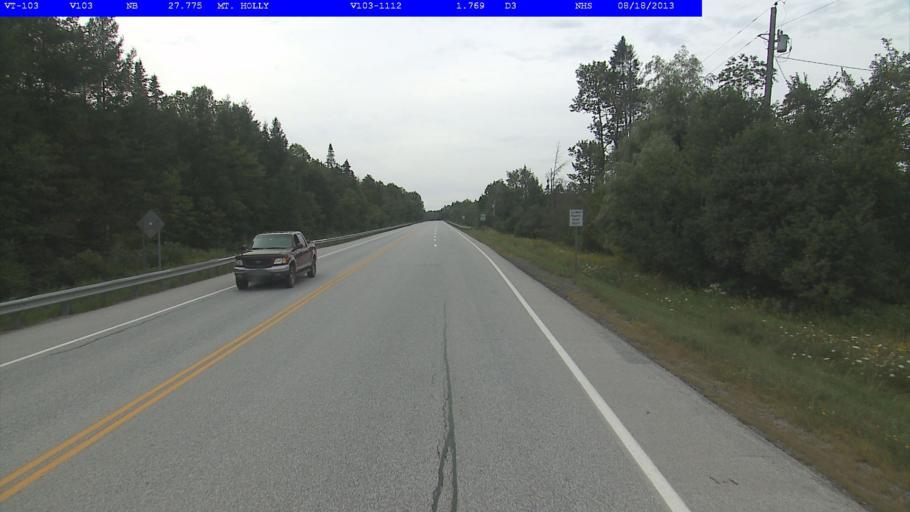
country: US
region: Vermont
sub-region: Windsor County
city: Chester
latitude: 43.4414
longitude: -72.7659
